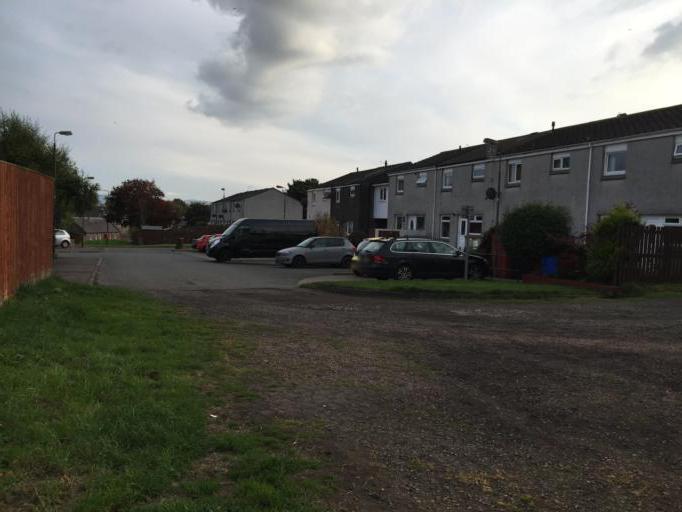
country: GB
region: Scotland
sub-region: West Lothian
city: Livingston
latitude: 55.9324
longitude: -3.5089
